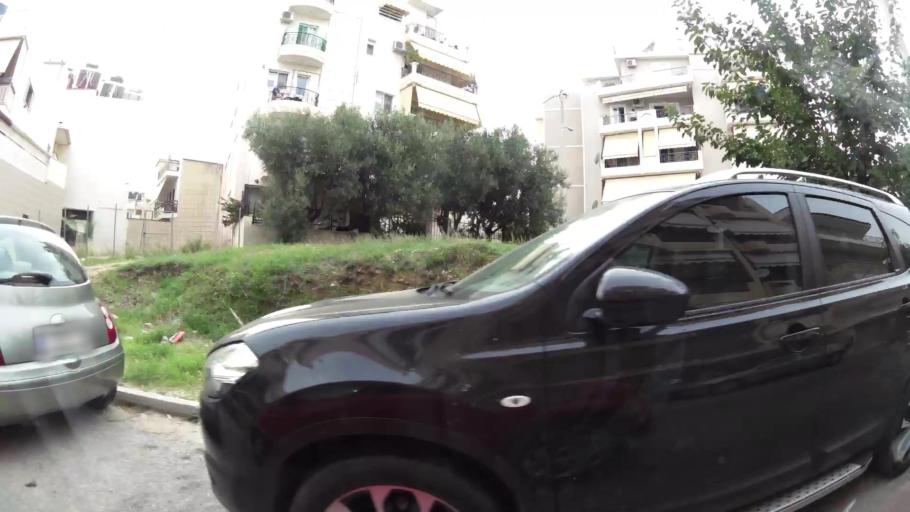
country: GR
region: Attica
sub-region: Nomarchia Athinas
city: Chaidari
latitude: 38.0126
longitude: 23.6712
